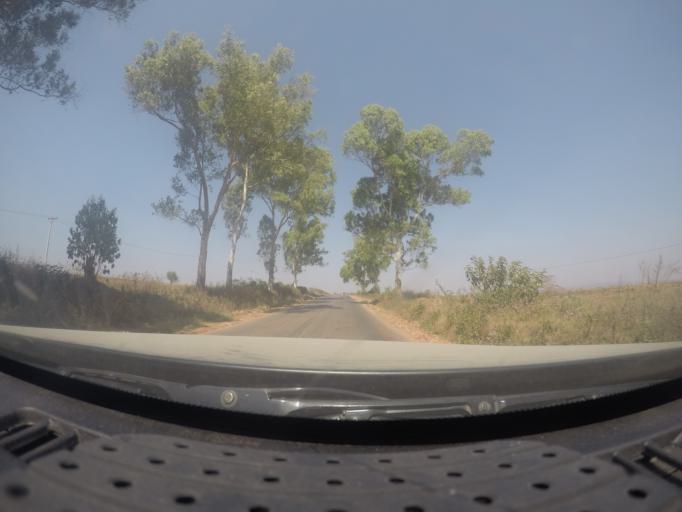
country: MM
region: Shan
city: Taunggyi
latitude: 20.7992
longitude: 96.6295
